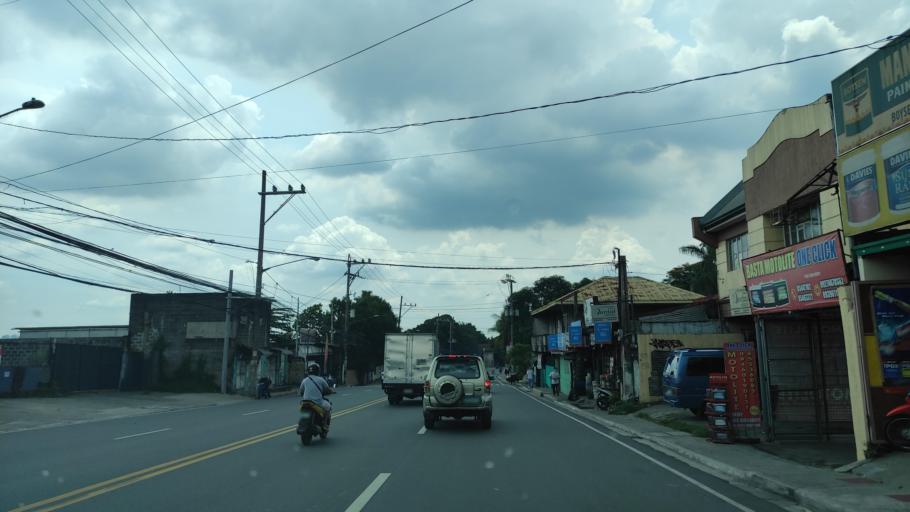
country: PH
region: Calabarzon
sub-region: Province of Rizal
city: Antipolo
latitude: 14.6188
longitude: 121.1302
